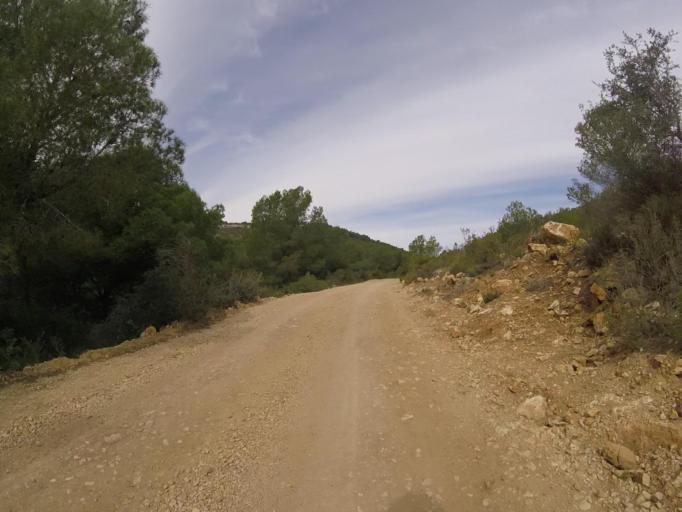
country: ES
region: Valencia
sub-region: Provincia de Castello
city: Cabanes
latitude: 40.1905
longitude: 0.0870
